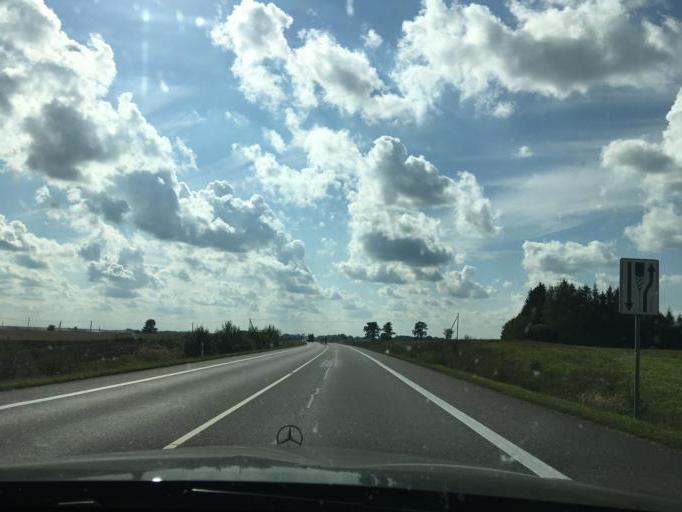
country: LT
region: Kauno apskritis
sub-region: Kauno rajonas
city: Mastaiciai
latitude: 54.7524
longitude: 23.7303
